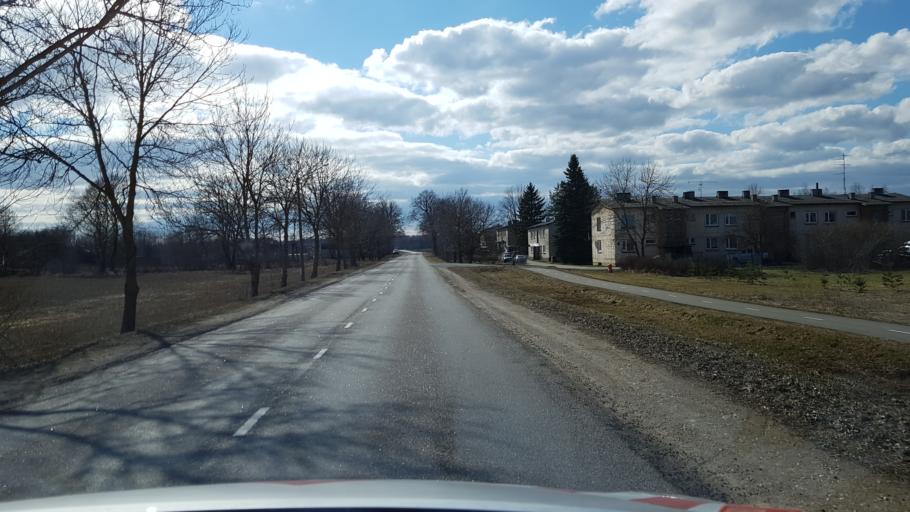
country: EE
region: Laeaene-Virumaa
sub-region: Rakvere linn
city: Rakvere
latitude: 59.3297
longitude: 26.2867
